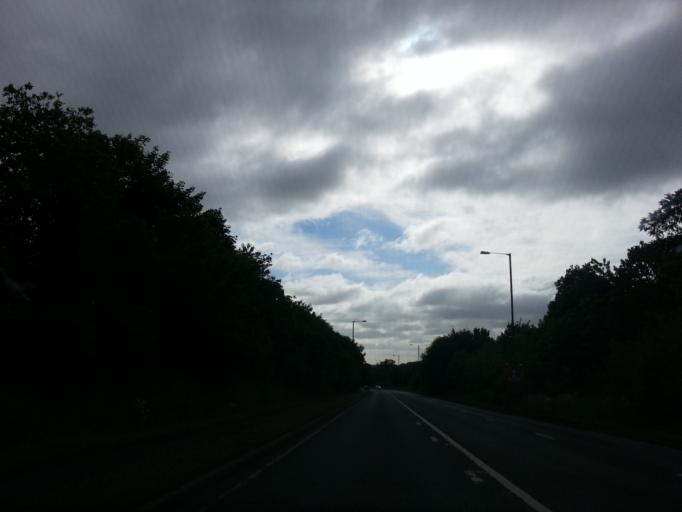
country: GB
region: England
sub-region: County Durham
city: Shildon
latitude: 54.6573
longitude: -1.6158
